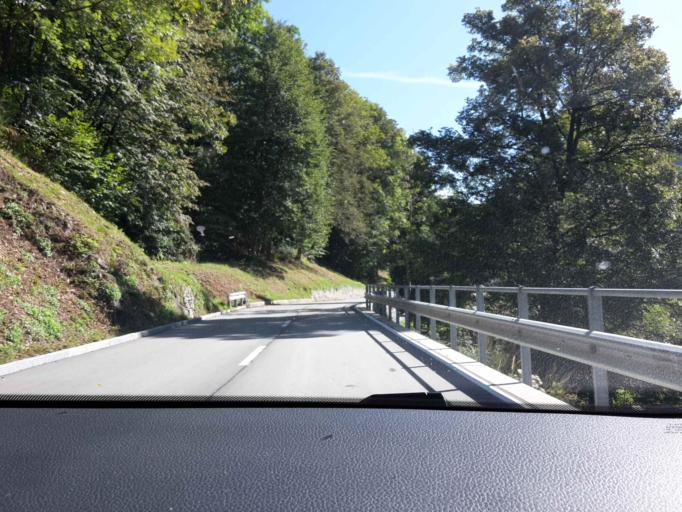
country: CH
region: Ticino
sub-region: Bellinzona District
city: Bellinzona
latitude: 46.1681
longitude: 9.0452
